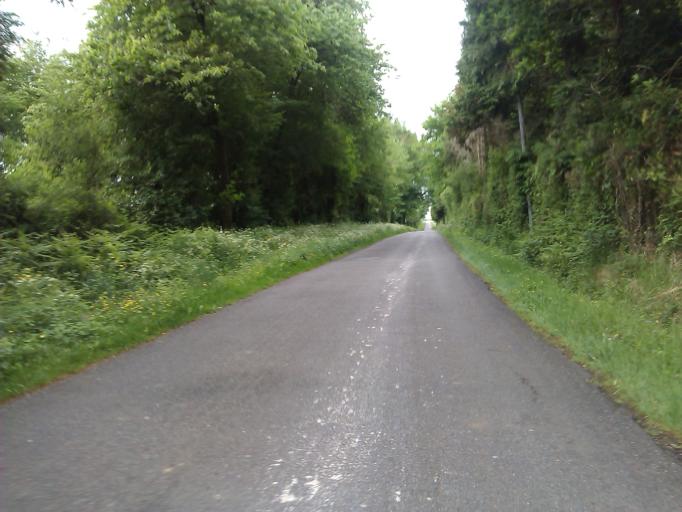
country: FR
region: Poitou-Charentes
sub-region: Departement de la Vienne
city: Charroux
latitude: 46.0983
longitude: 0.5167
